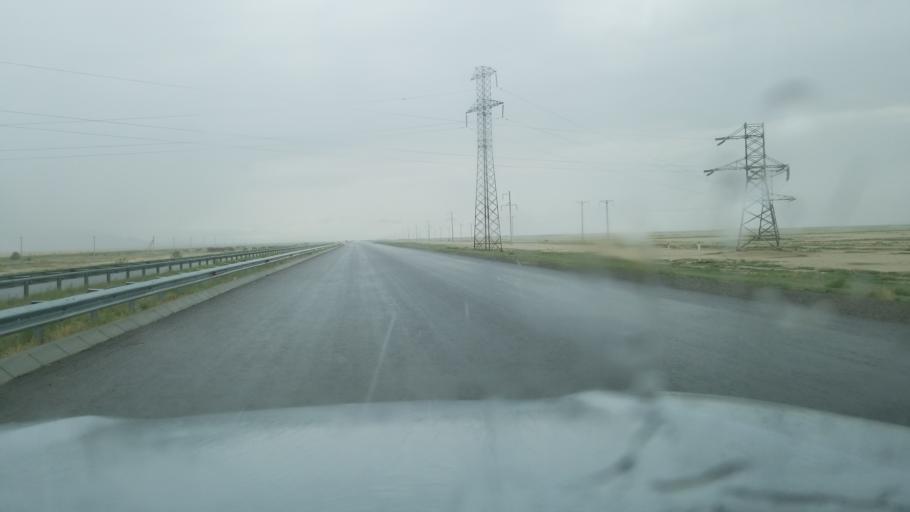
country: TM
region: Balkan
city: Serdar
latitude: 39.0212
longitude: 56.2075
